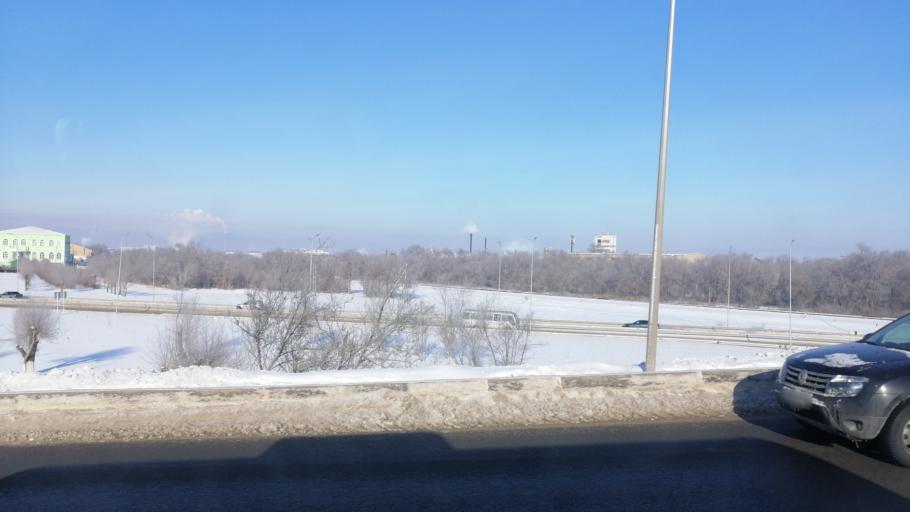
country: KZ
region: Aqtoebe
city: Aqtobe
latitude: 50.2946
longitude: 57.1780
